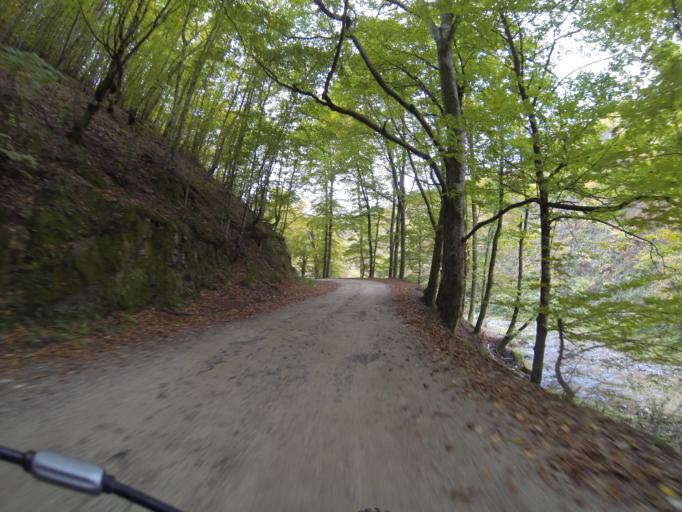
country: RO
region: Gorj
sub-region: Comuna Tismana
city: Sohodol
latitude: 45.0618
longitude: 22.8971
